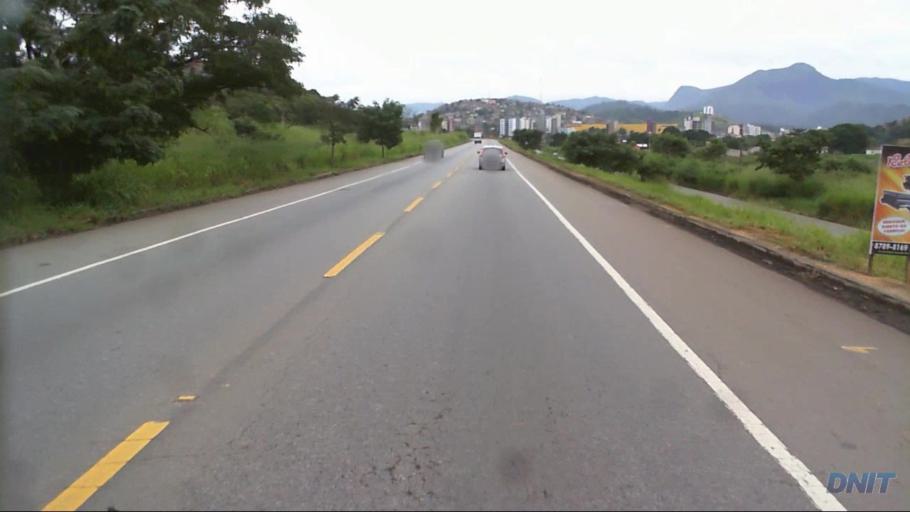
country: BR
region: Minas Gerais
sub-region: Coronel Fabriciano
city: Coronel Fabriciano
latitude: -19.5299
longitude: -42.6121
